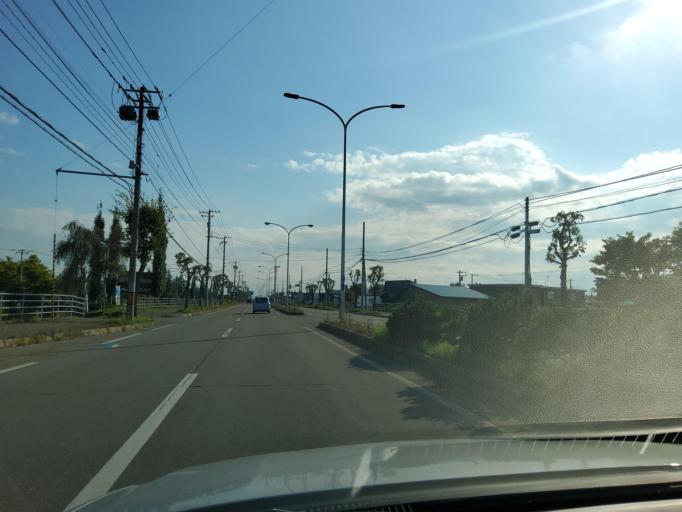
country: JP
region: Hokkaido
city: Obihiro
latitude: 42.8866
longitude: 143.2033
